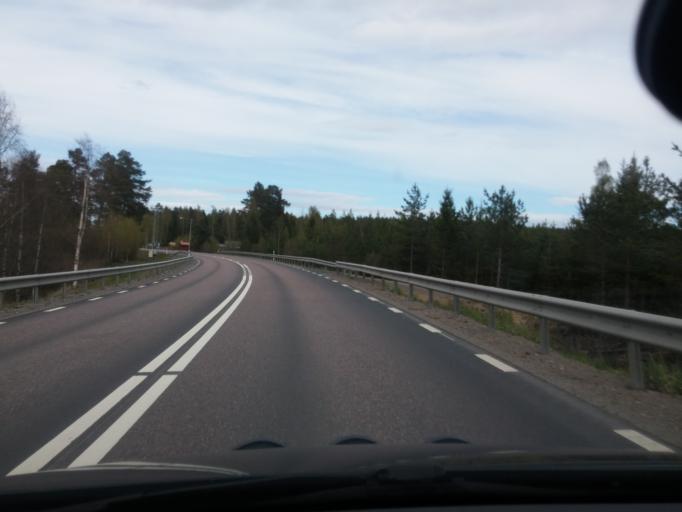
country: SE
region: Gaevleborg
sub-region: Ljusdals Kommun
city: Ljusdal
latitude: 61.8184
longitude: 16.0230
